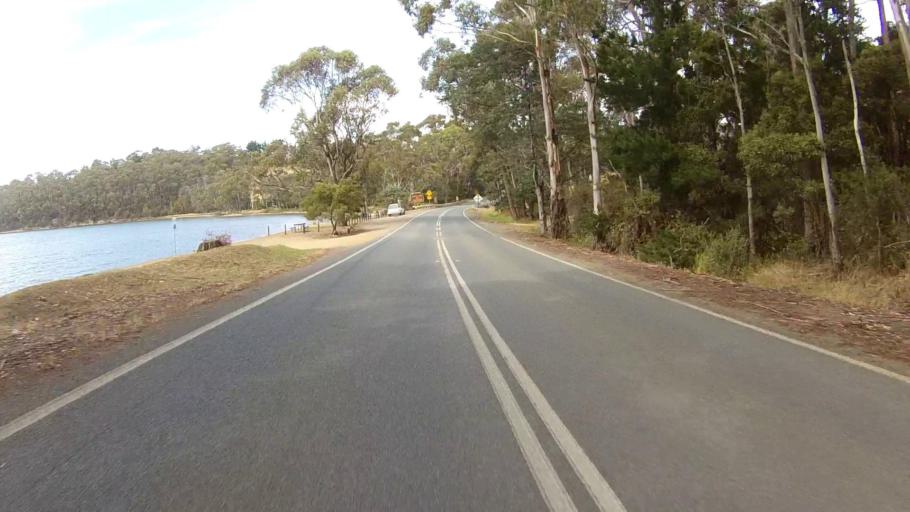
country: AU
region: Tasmania
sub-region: Kingborough
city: Kettering
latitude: -43.1326
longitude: 147.2522
